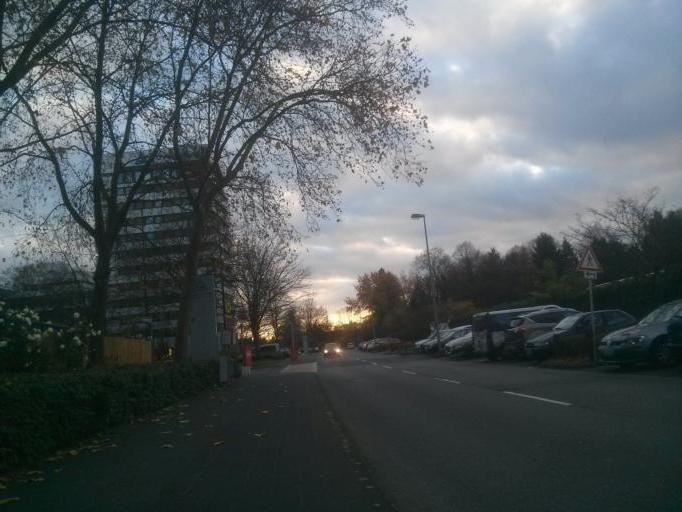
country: DE
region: North Rhine-Westphalia
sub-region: Regierungsbezirk Koln
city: Humboldtkolonie
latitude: 50.9243
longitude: 6.9916
